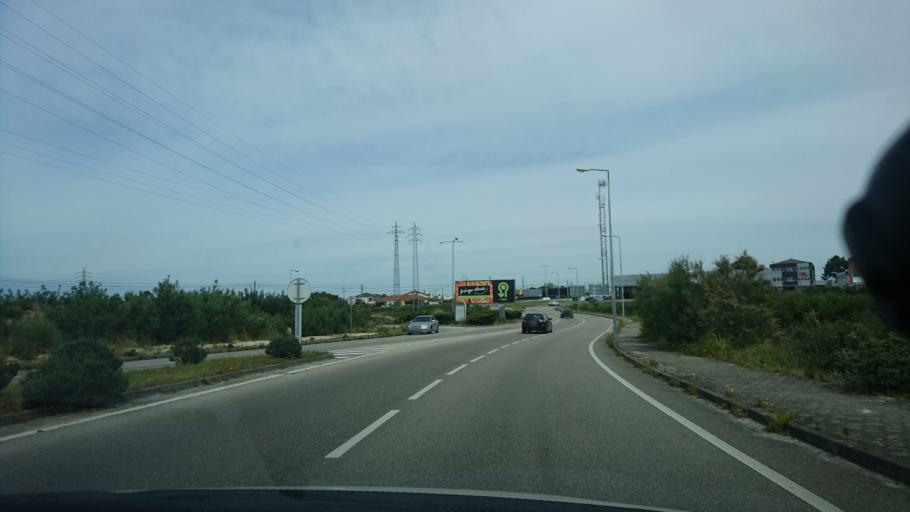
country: PT
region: Aveiro
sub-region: Aveiro
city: Aveiro
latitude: 40.6516
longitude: -8.6169
